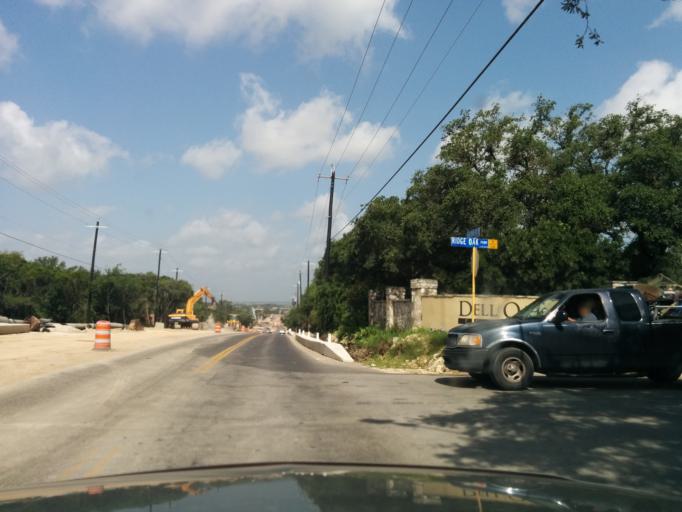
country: US
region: Texas
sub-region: Bexar County
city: Helotes
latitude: 29.5723
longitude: -98.6244
